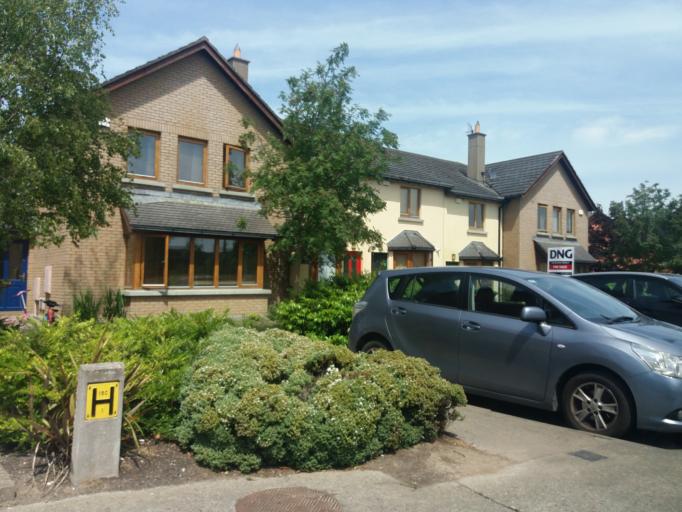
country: IE
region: Leinster
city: Lusk
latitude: 53.5289
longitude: -6.1616
